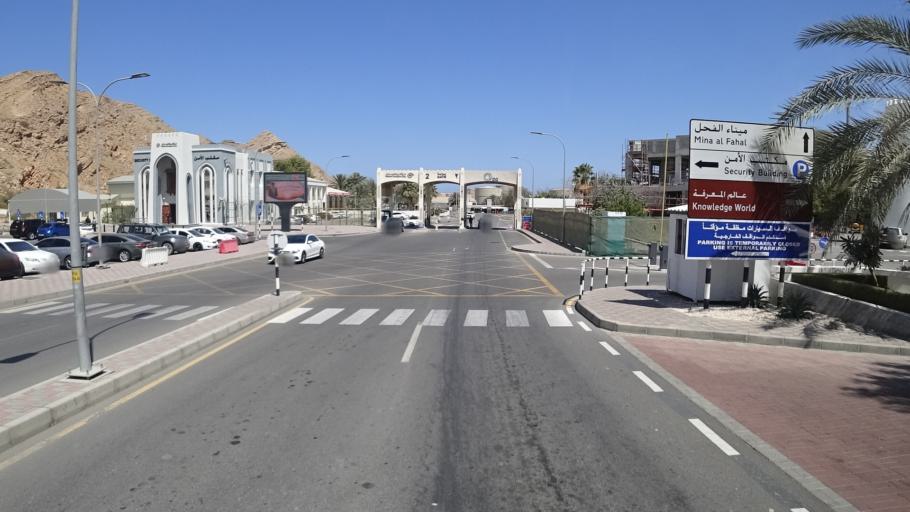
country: OM
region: Muhafazat Masqat
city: Muscat
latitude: 23.6252
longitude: 58.5082
